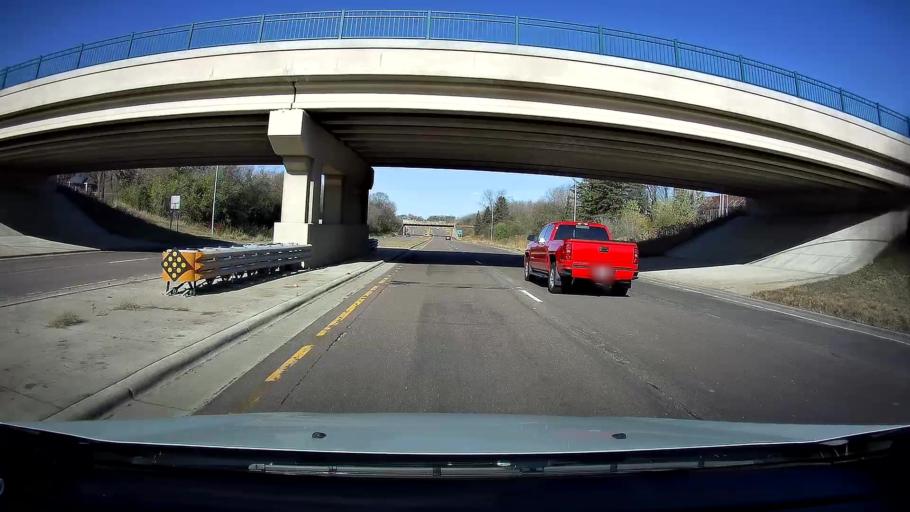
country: US
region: Minnesota
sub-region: Ramsey County
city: Arden Hills
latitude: 45.0499
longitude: -93.1567
